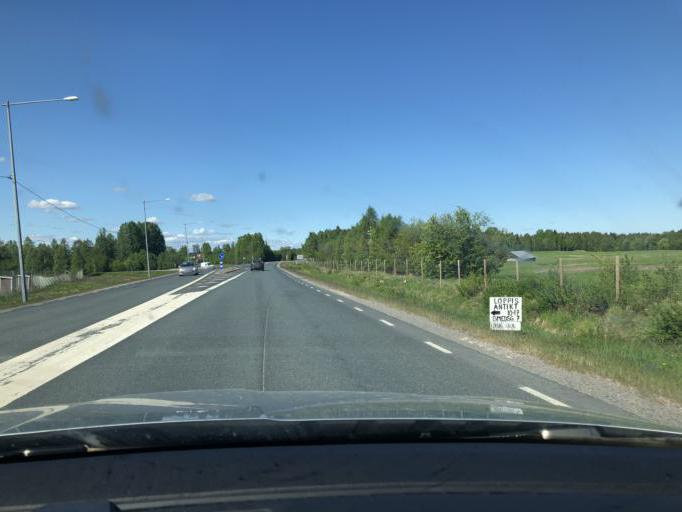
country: SE
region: Norrbotten
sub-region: Kalix Kommun
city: Kalix
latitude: 65.8405
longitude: 23.1935
